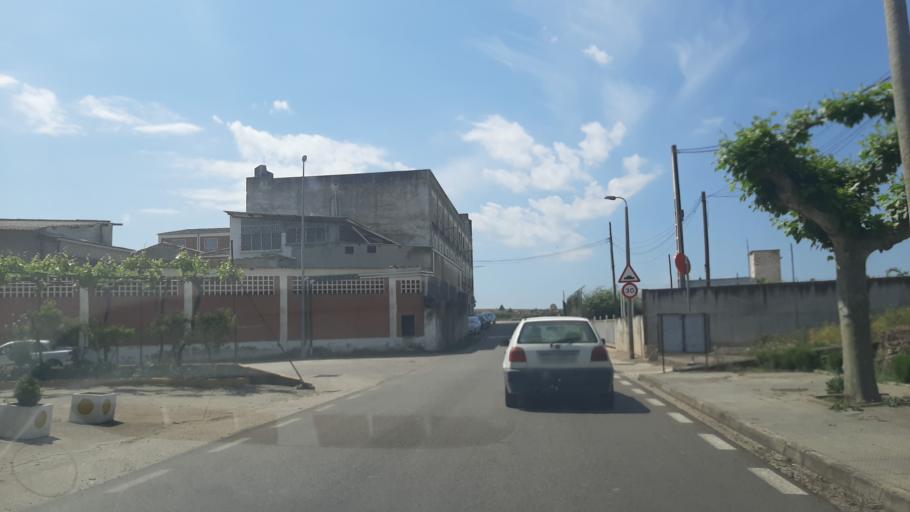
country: ES
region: Castille and Leon
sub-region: Provincia de Salamanca
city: Gallegos de Arganan
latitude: 40.6271
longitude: -6.7037
